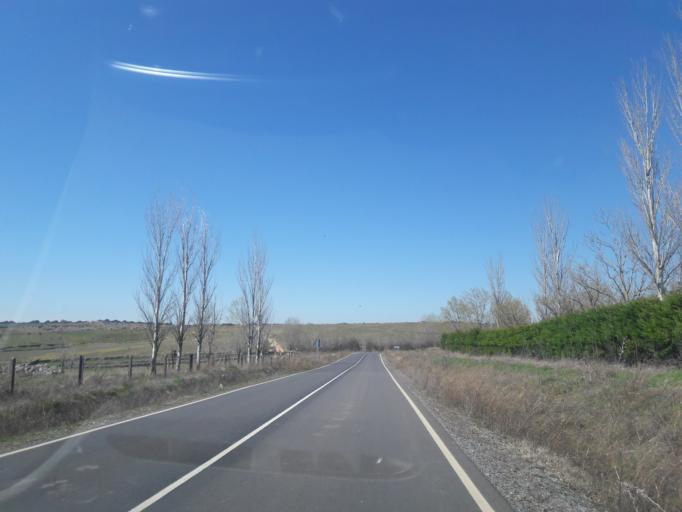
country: ES
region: Castille and Leon
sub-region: Provincia de Salamanca
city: Martinamor
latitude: 40.8071
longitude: -5.6078
